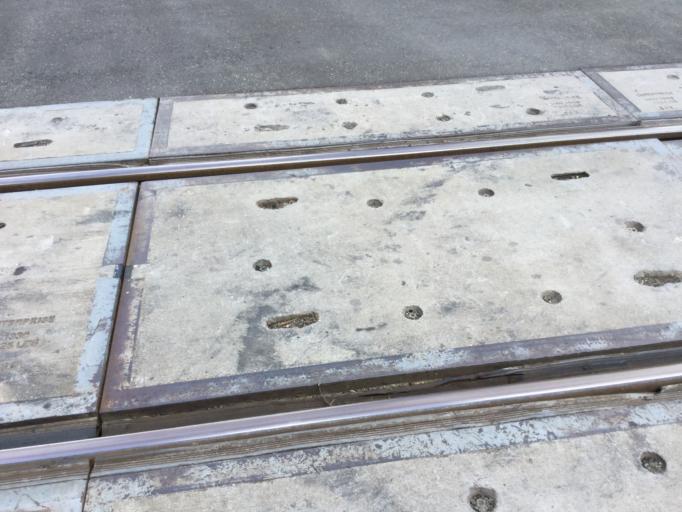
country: US
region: Kansas
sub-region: Labette County
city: Oswego
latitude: 37.1643
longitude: -95.1293
